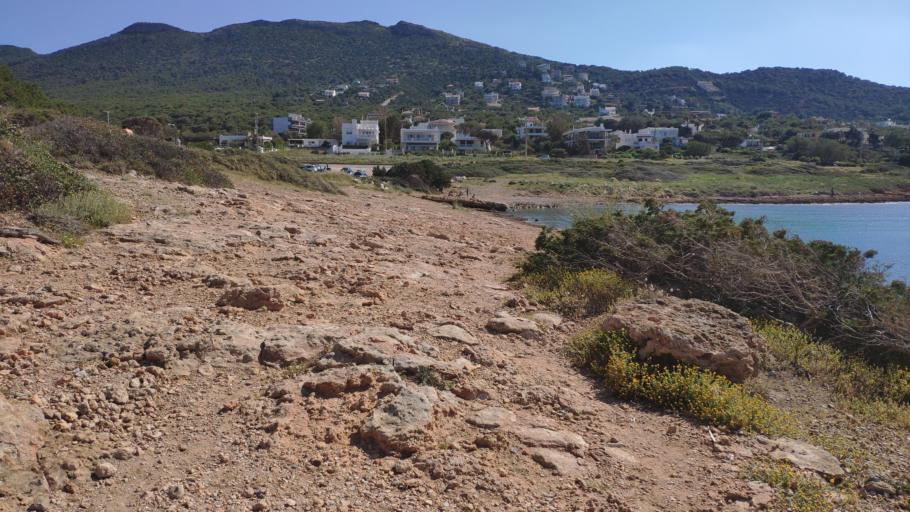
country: GR
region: Attica
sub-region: Nomarchia Anatolikis Attikis
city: Limin Mesoyaias
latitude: 37.9224
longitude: 24.0277
